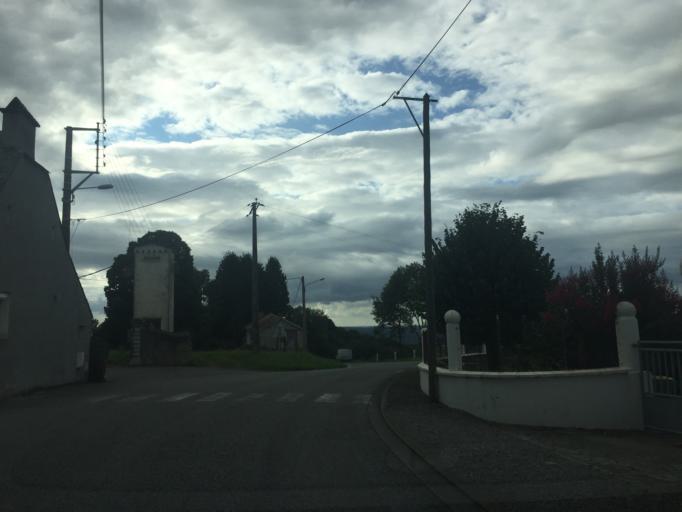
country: FR
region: Midi-Pyrenees
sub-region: Departement des Hautes-Pyrenees
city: Capvern
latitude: 43.1035
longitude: 0.3106
